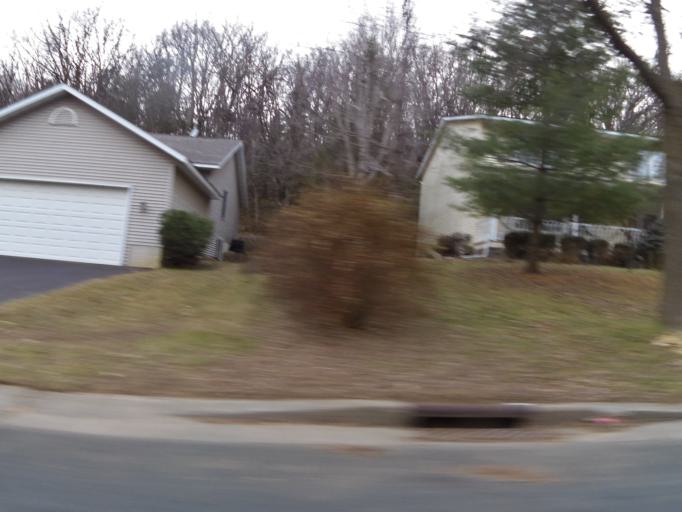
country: US
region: Wisconsin
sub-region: Pierce County
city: River Falls
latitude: 44.8600
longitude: -92.5977
